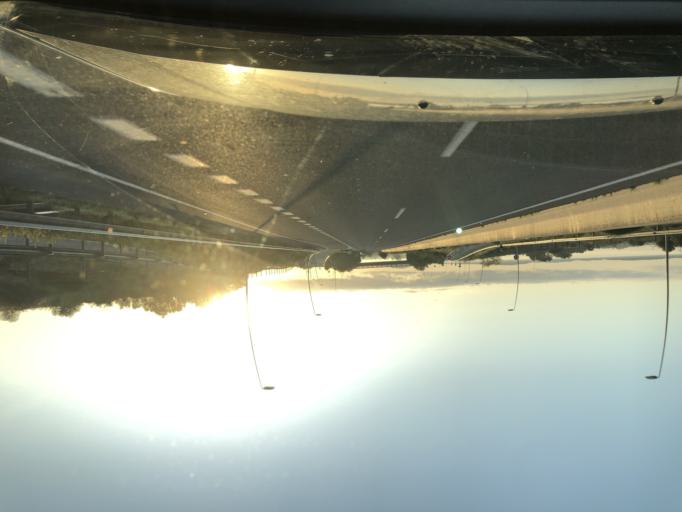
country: ES
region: Balearic Islands
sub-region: Illes Balears
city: Algaida
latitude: 39.5667
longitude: 2.9308
